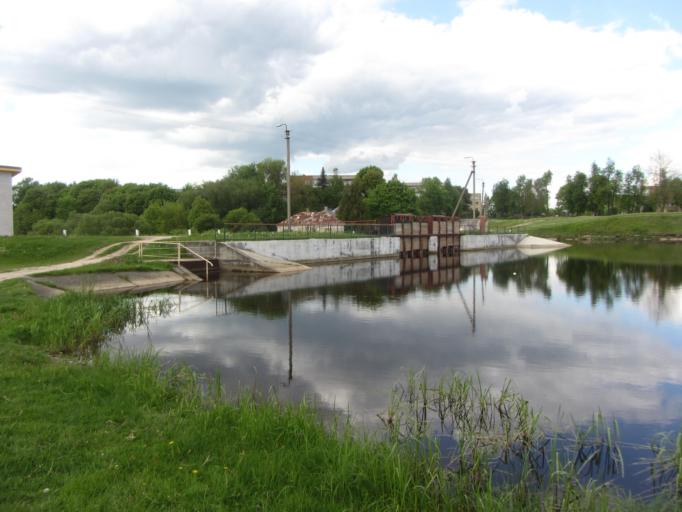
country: LT
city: Sirvintos
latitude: 55.0463
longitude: 24.9544
